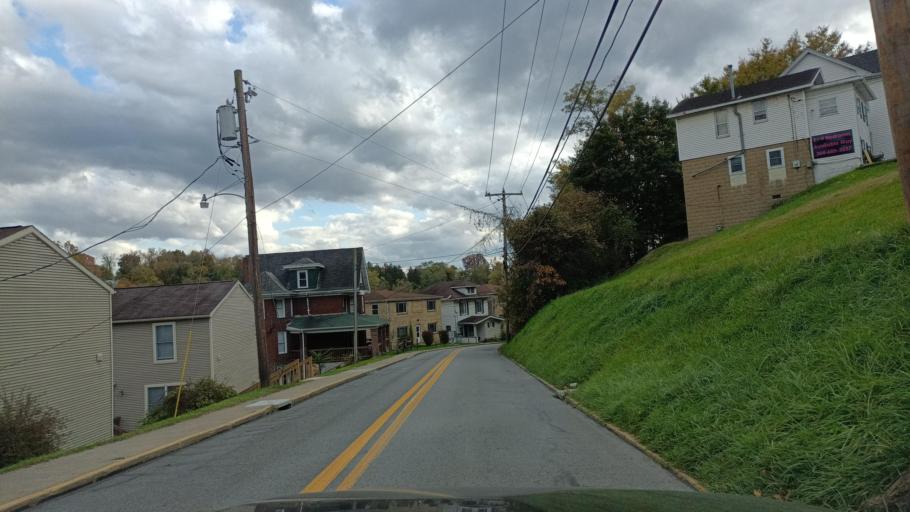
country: US
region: West Virginia
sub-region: Monongalia County
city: Morgantown
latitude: 39.6413
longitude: -79.9503
